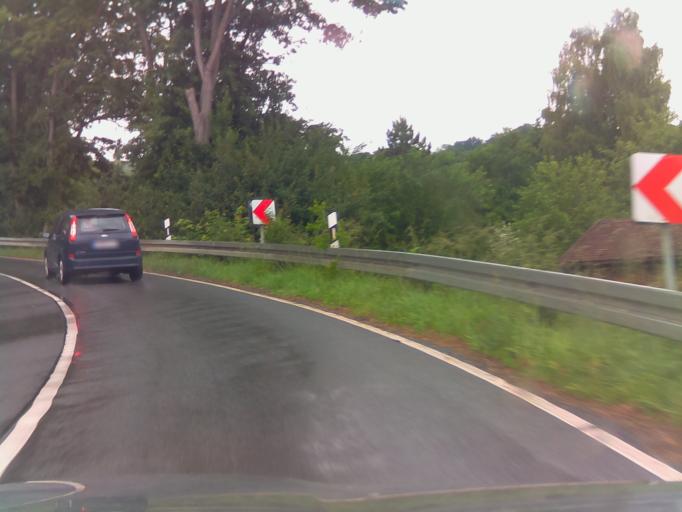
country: DE
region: Hesse
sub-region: Regierungsbezirk Darmstadt
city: Brensbach
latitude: 49.8073
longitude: 8.8876
